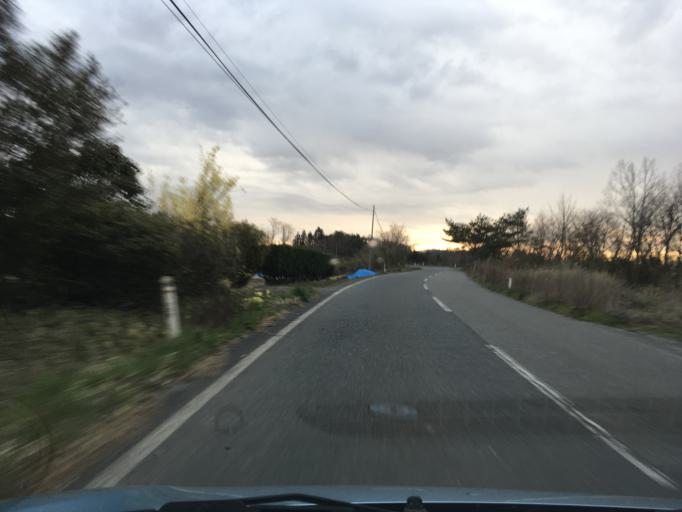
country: JP
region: Iwate
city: Ichinoseki
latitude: 38.7774
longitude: 141.2439
